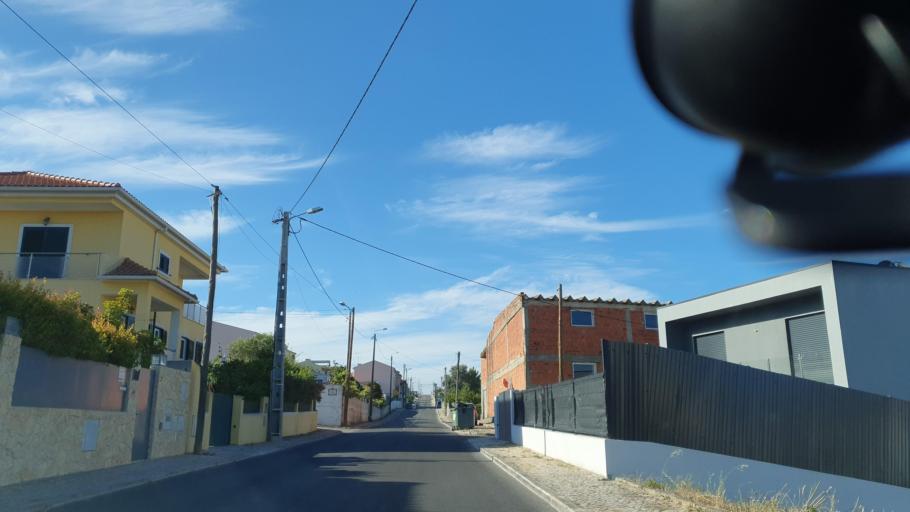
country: PT
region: Lisbon
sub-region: Sintra
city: Belas
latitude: 38.7968
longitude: -9.2533
